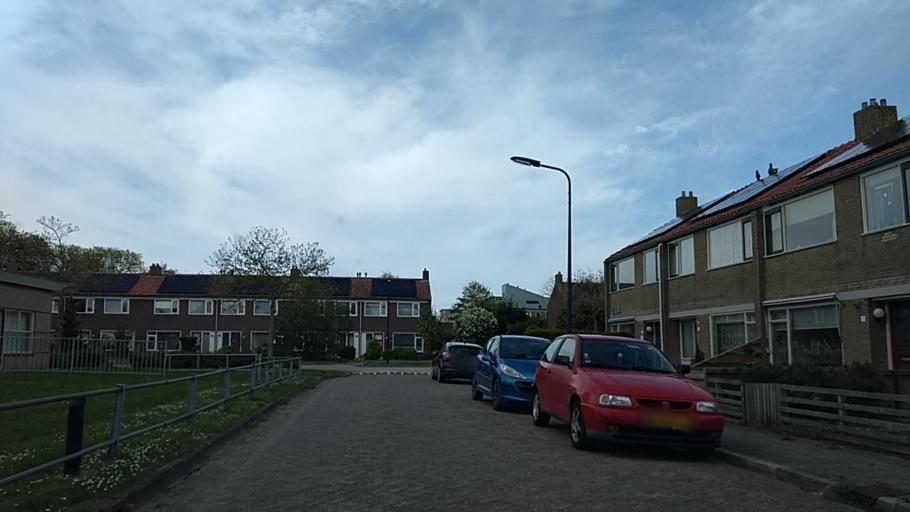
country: NL
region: Friesland
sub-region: Gemeente Harlingen
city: Harlingen
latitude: 53.1663
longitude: 5.4361
